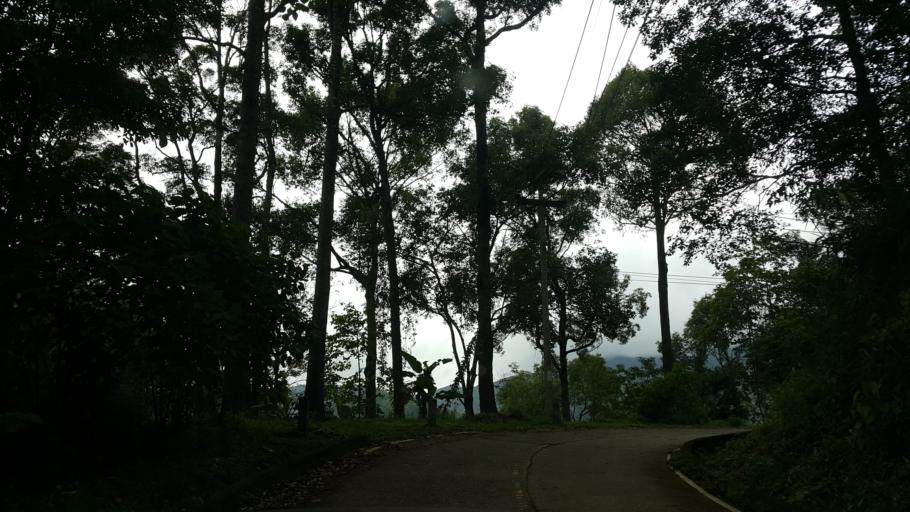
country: TH
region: Lampang
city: Mueang Pan
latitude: 18.8264
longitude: 99.3907
